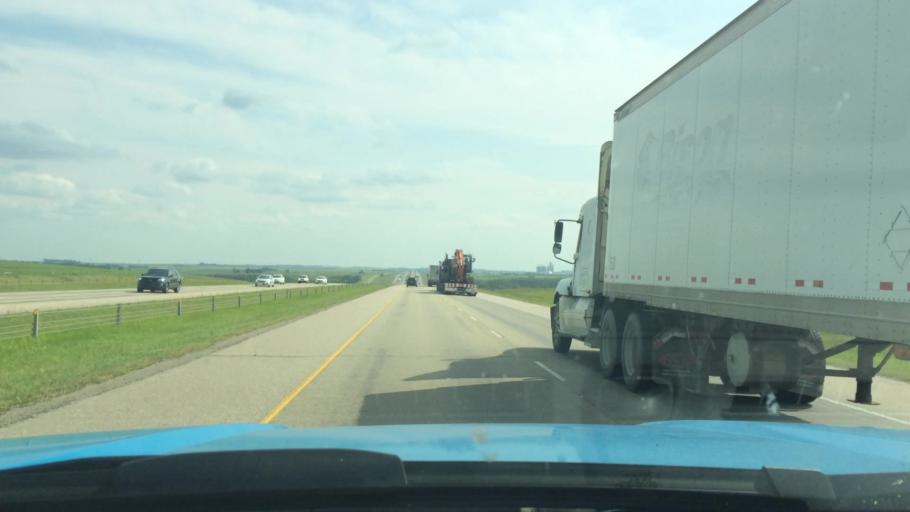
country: CA
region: Alberta
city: Carstairs
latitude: 51.5257
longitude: -114.0251
